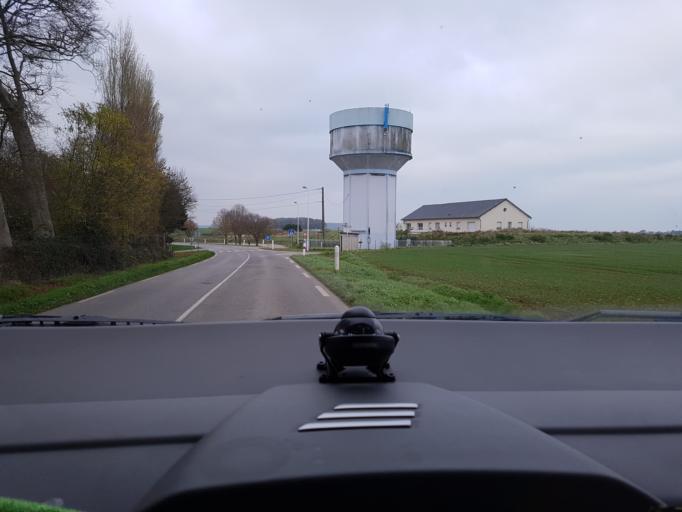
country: FR
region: Haute-Normandie
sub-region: Departement de la Seine-Maritime
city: Le Treport
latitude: 50.0297
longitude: 1.3517
